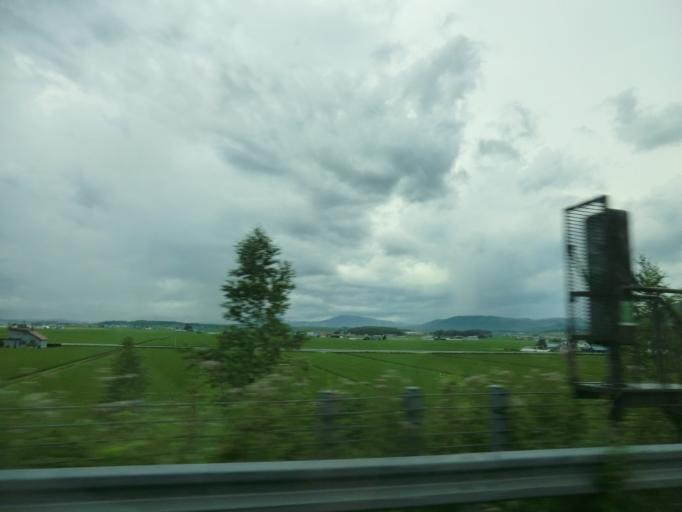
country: JP
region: Hokkaido
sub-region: Asahikawa-shi
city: Asahikawa
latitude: 43.8508
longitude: 142.4266
